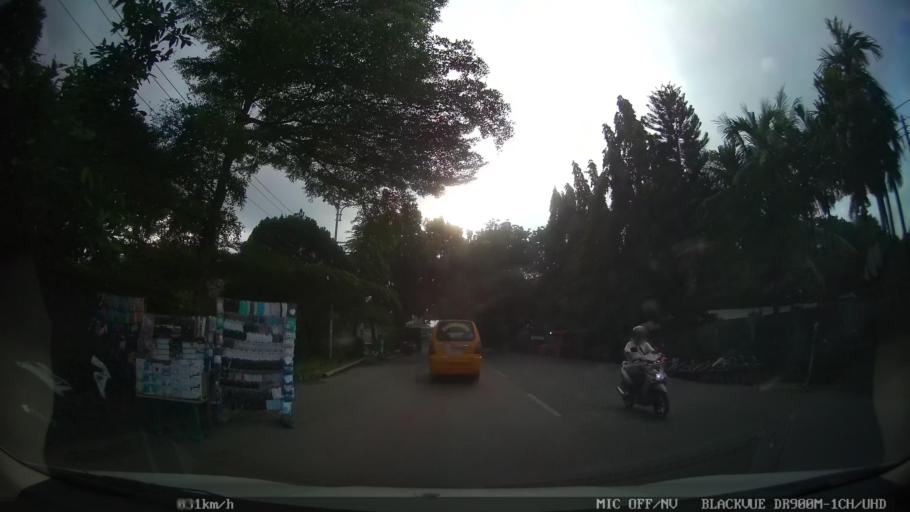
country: ID
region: North Sumatra
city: Medan
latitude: 3.5969
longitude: 98.7417
